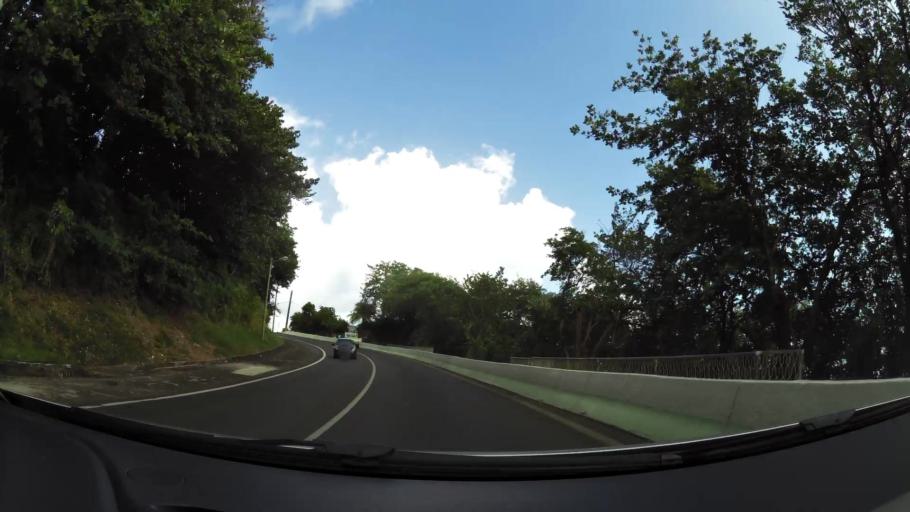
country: MQ
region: Martinique
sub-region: Martinique
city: Le Lorrain
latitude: 14.8266
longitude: -61.0314
